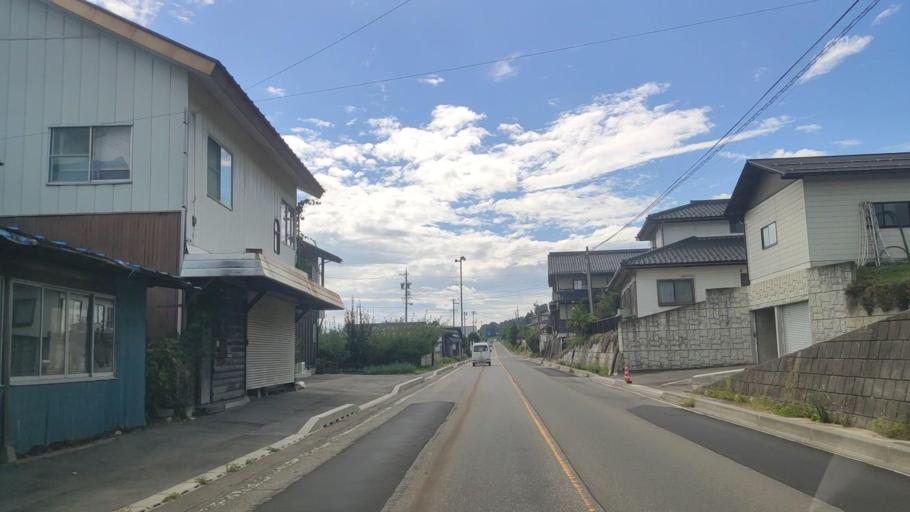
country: JP
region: Nagano
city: Nakano
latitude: 36.7653
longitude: 138.3189
